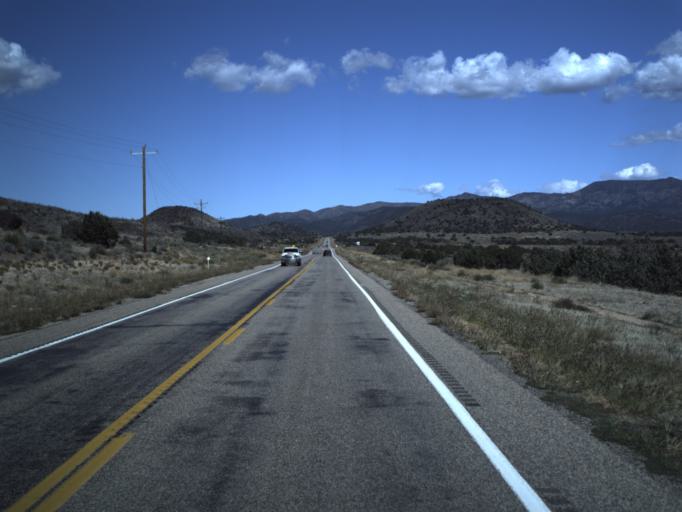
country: US
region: Utah
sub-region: Washington County
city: Enterprise
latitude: 37.3762
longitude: -113.6557
